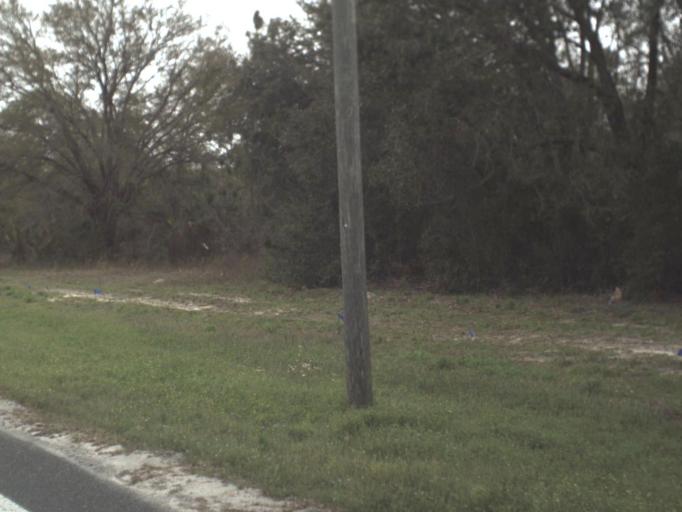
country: US
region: Florida
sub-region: Wakulla County
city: Crawfordville
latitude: 30.1072
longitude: -84.3787
